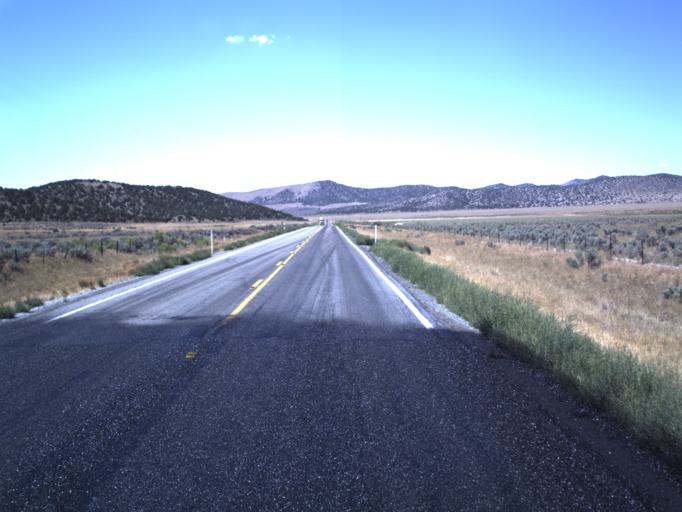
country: US
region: Utah
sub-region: Juab County
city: Nephi
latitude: 39.6975
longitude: -111.9661
